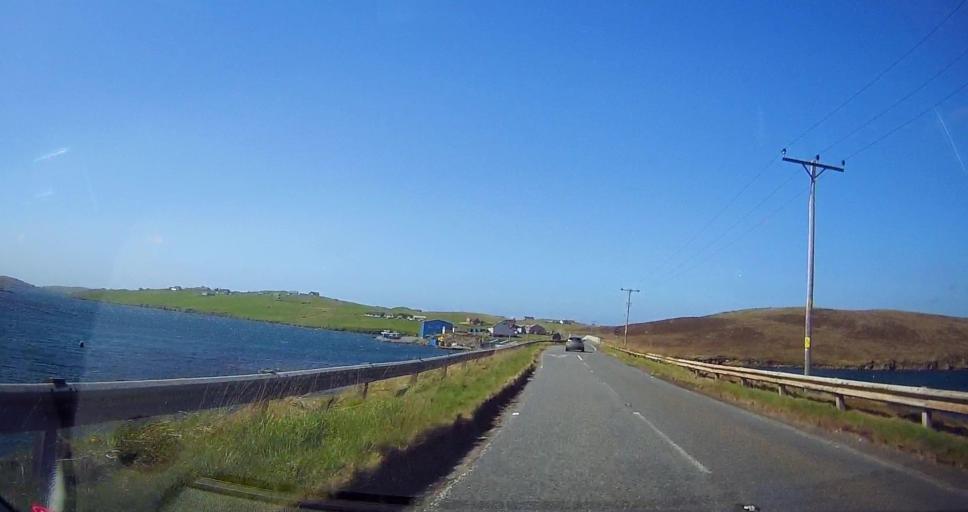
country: GB
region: Scotland
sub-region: Shetland Islands
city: Sandwick
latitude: 60.1059
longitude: -1.3053
